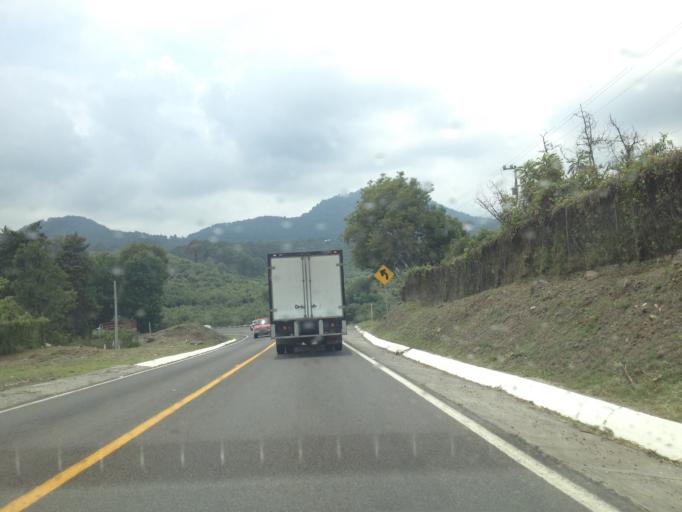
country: MX
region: Michoacan
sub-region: Uruapan
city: Toreo Bajo (El Toreo Bajo)
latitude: 19.4580
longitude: -101.9963
